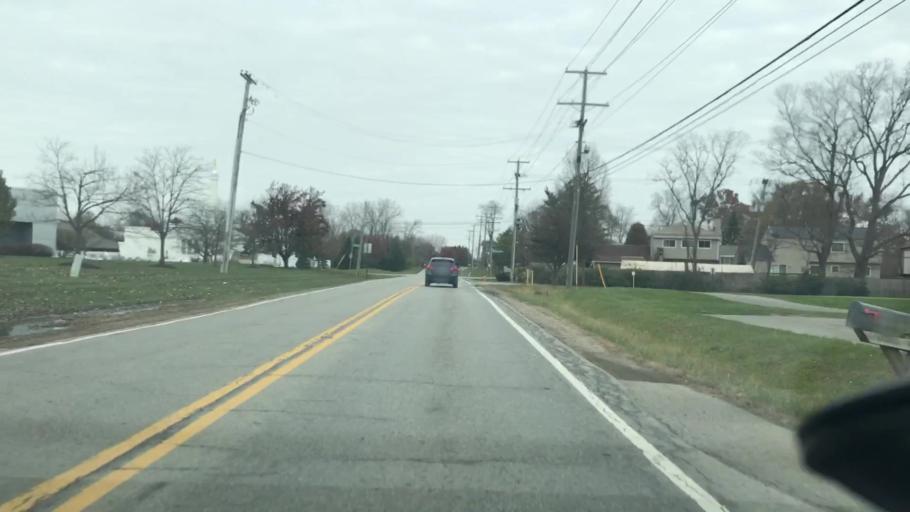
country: US
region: Ohio
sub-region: Franklin County
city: Lincoln Village
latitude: 39.9931
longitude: -83.1115
